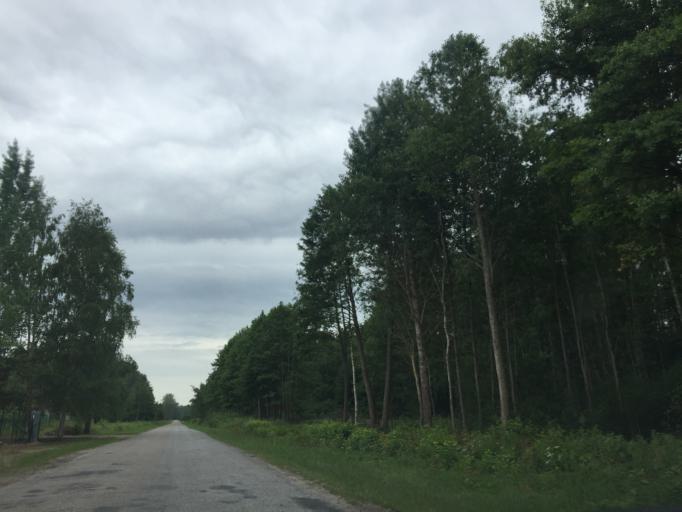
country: LV
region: Tukuma Rajons
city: Engure
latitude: 57.1217
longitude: 23.2277
